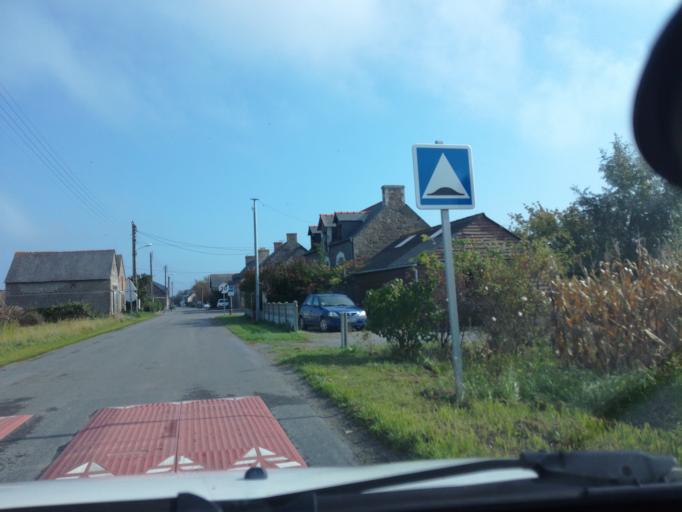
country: FR
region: Brittany
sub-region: Departement d'Ille-et-Vilaine
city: Cherrueix
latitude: 48.6069
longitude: -1.7009
